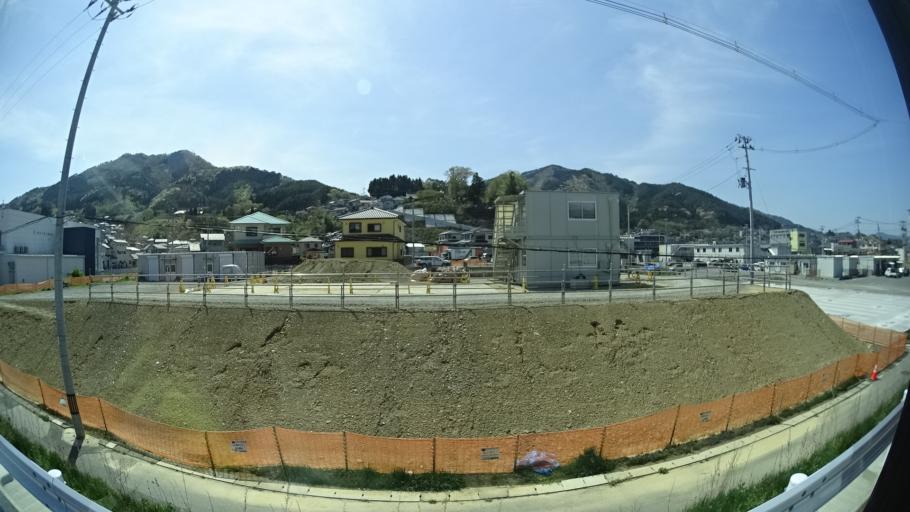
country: JP
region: Iwate
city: Ofunato
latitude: 39.0591
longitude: 141.7208
